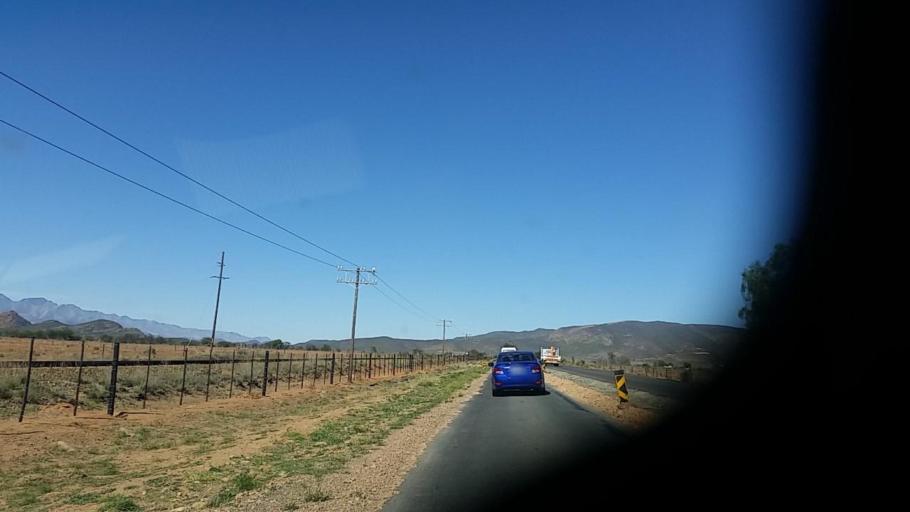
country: ZA
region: Western Cape
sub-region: Eden District Municipality
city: Oudtshoorn
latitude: -33.5612
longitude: 22.3998
